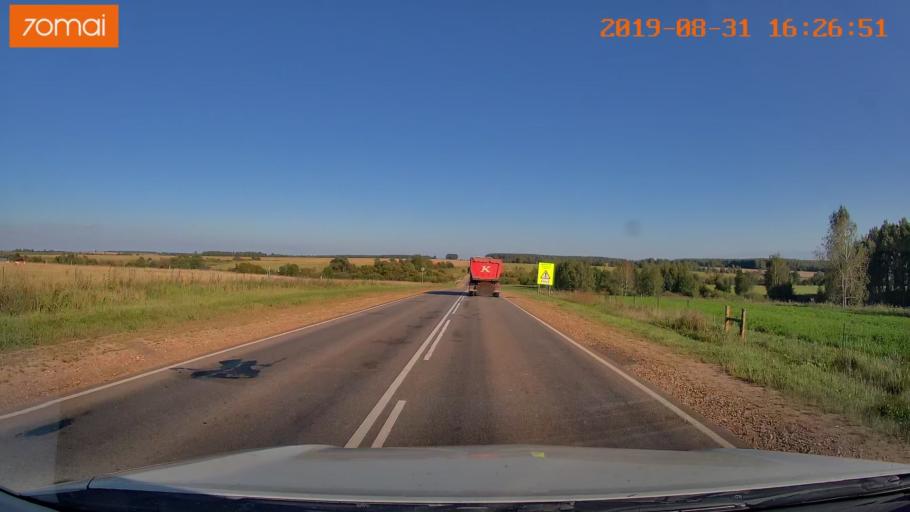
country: RU
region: Kaluga
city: Babynino
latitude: 54.5163
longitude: 35.7429
